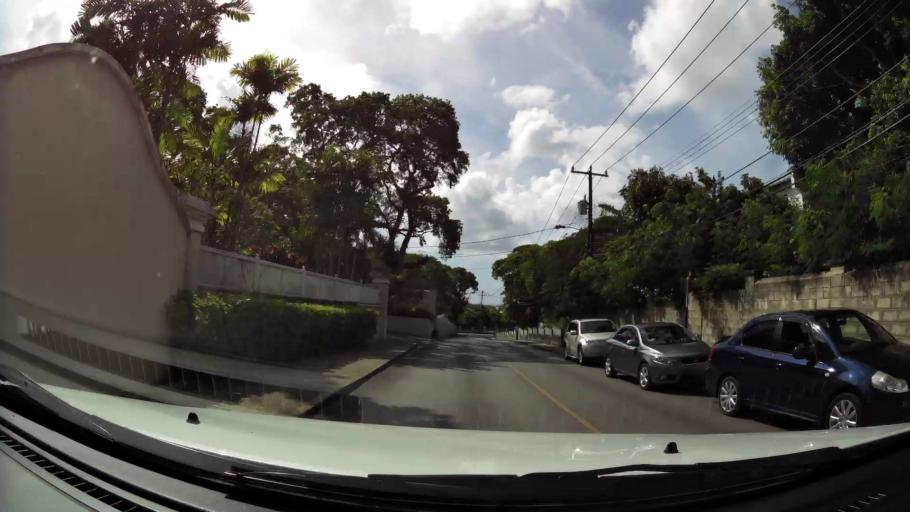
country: BB
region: Saint Michael
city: Bridgetown
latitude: 13.1001
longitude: -59.5989
